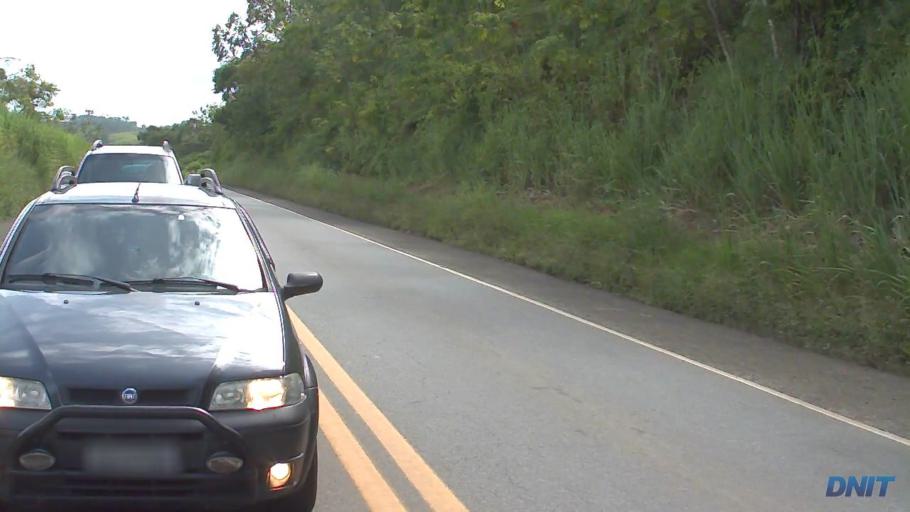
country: BR
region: Minas Gerais
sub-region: Ipaba
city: Ipaba
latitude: -19.3735
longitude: -42.4608
